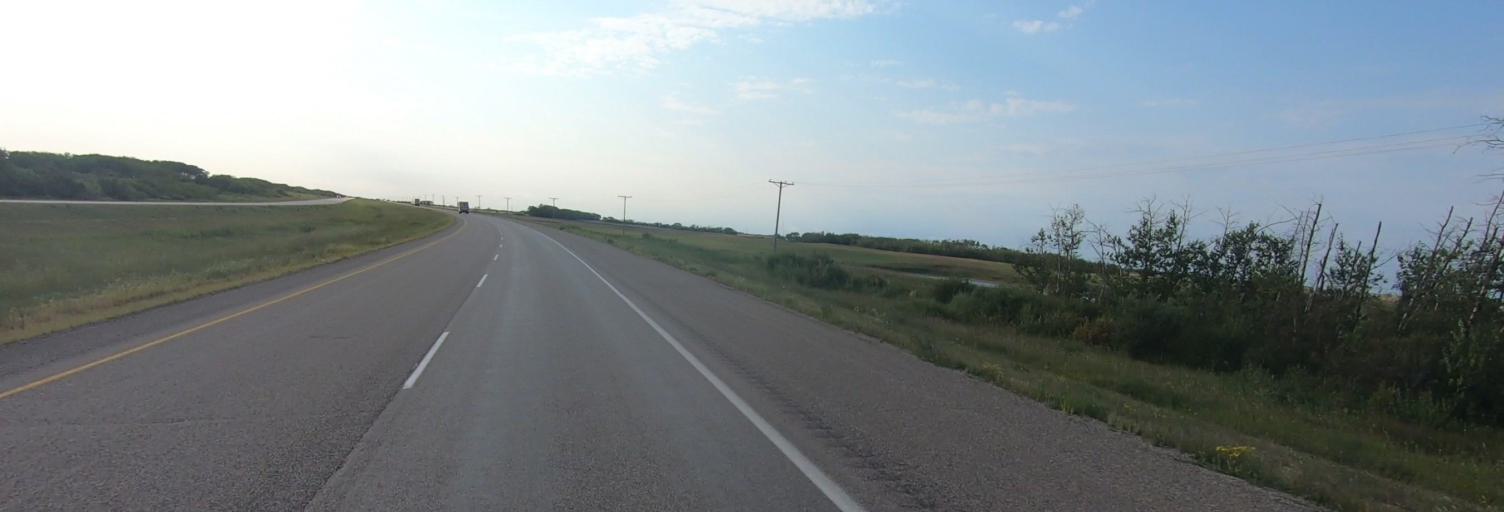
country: CA
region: Saskatchewan
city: Esterhazy
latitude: 50.3543
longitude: -102.3391
